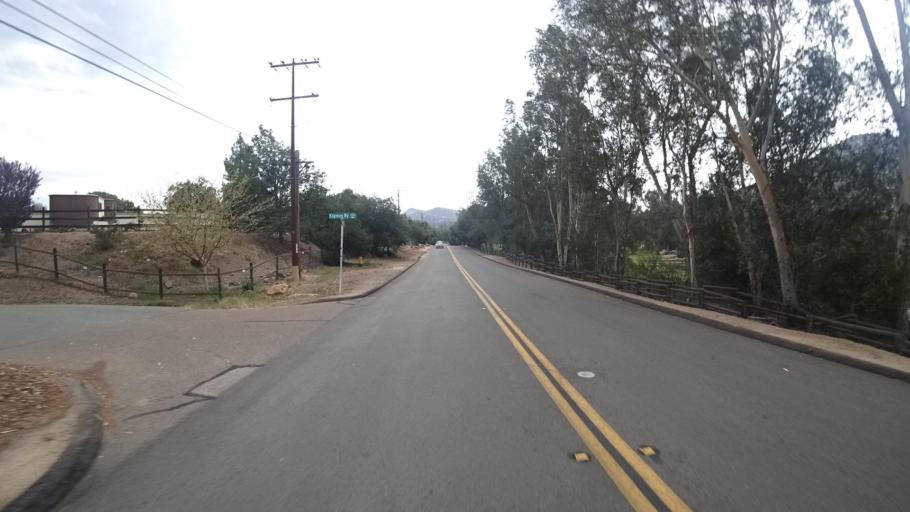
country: US
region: California
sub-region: San Diego County
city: San Pasqual
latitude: 33.0172
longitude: -116.9532
